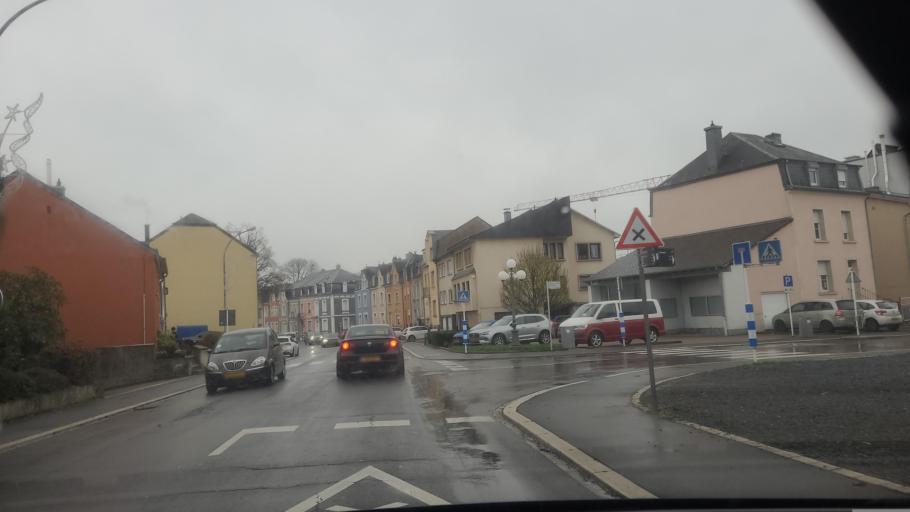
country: LU
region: Luxembourg
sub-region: Canton de Capellen
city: Bascharage
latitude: 49.5671
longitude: 5.9065
